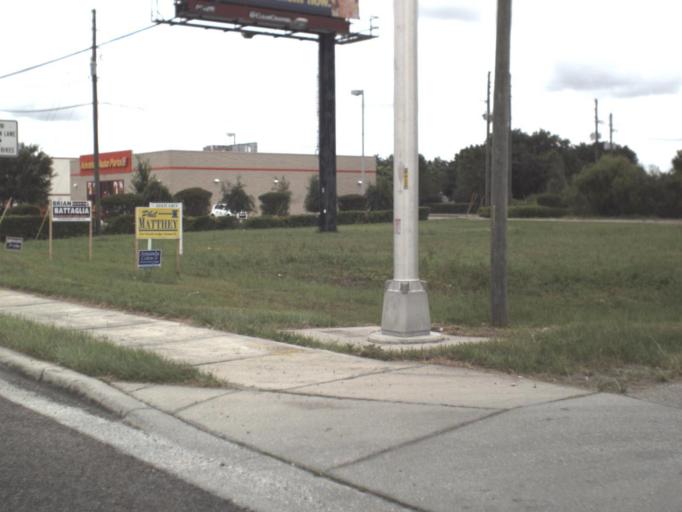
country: US
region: Florida
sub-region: Hillsborough County
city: Keystone
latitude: 28.1928
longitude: -82.6329
